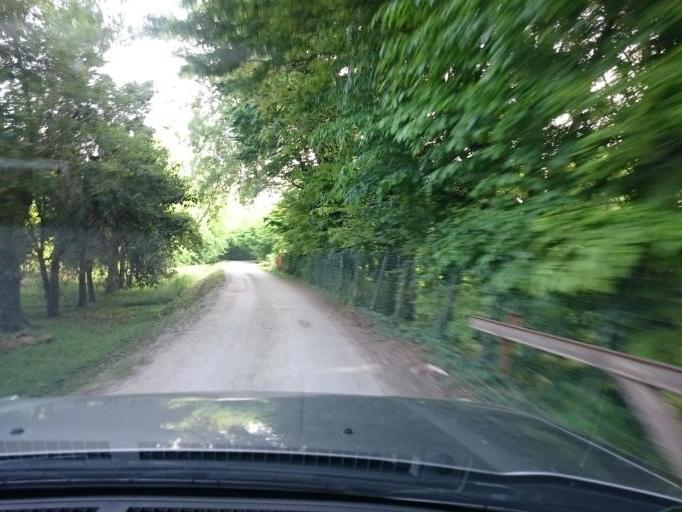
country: IT
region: Veneto
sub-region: Provincia di Padova
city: Ponte San Nicolo
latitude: 45.3980
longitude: 11.9219
